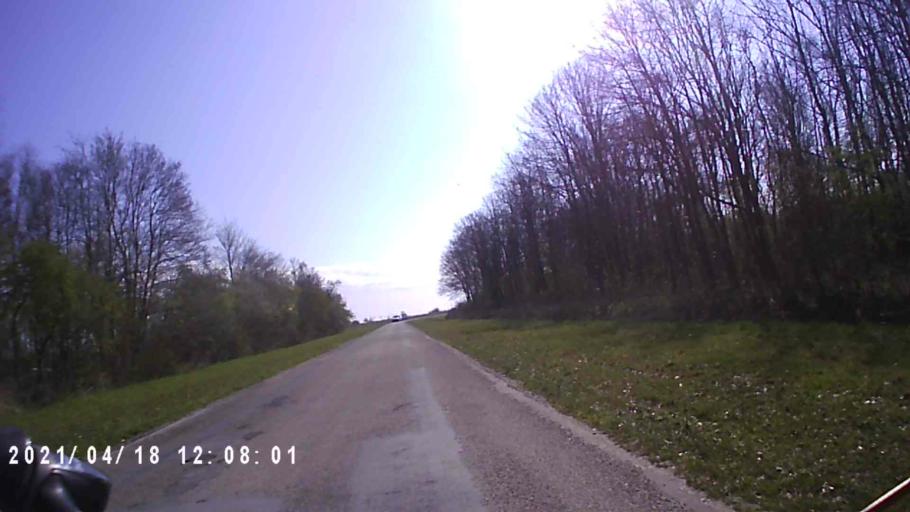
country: NL
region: Friesland
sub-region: Gemeente Kollumerland en Nieuwkruisland
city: Kollum
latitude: 53.3238
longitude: 6.1891
